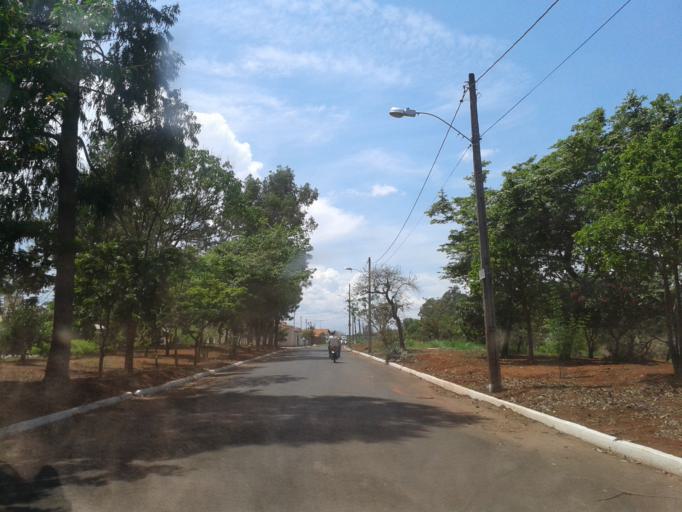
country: BR
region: Minas Gerais
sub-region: Araguari
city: Araguari
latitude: -18.6745
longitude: -48.1829
